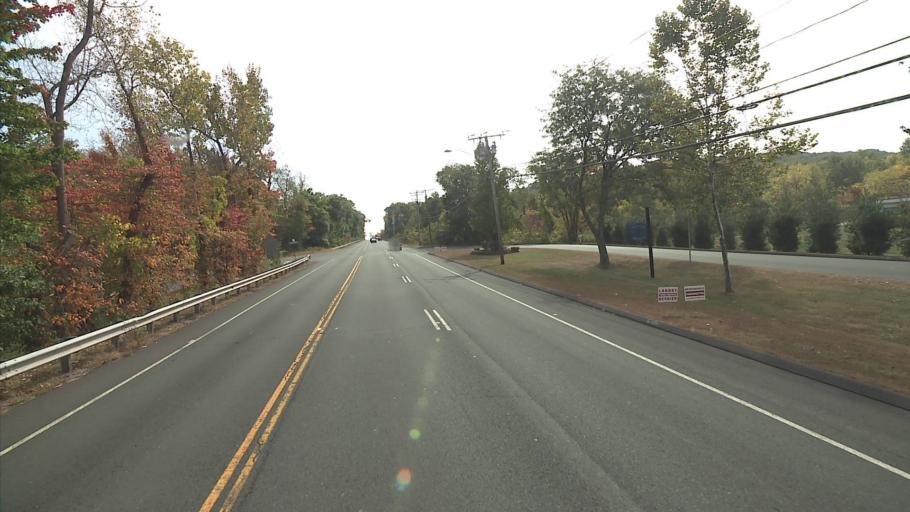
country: US
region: Connecticut
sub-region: Hartford County
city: Farmington
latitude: 41.7100
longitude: -72.8305
